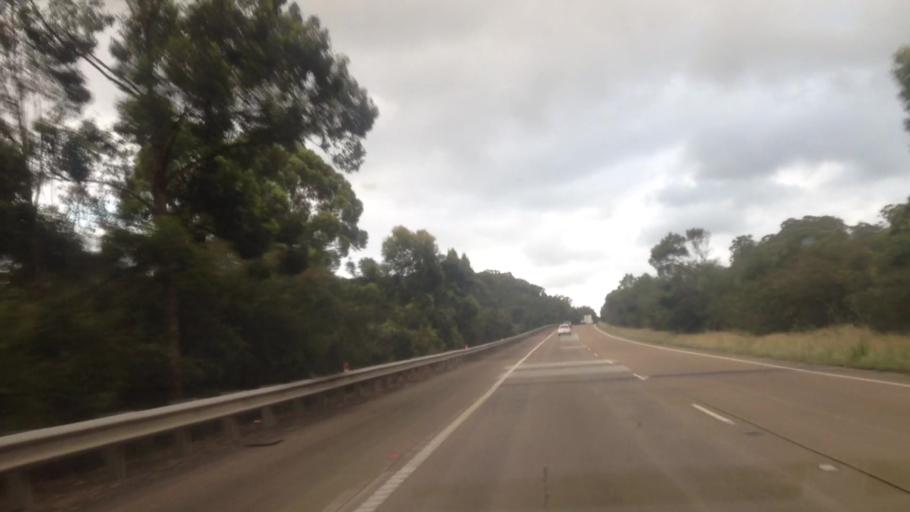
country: AU
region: New South Wales
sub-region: Wyong Shire
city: Charmhaven
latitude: -33.1559
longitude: 151.4708
